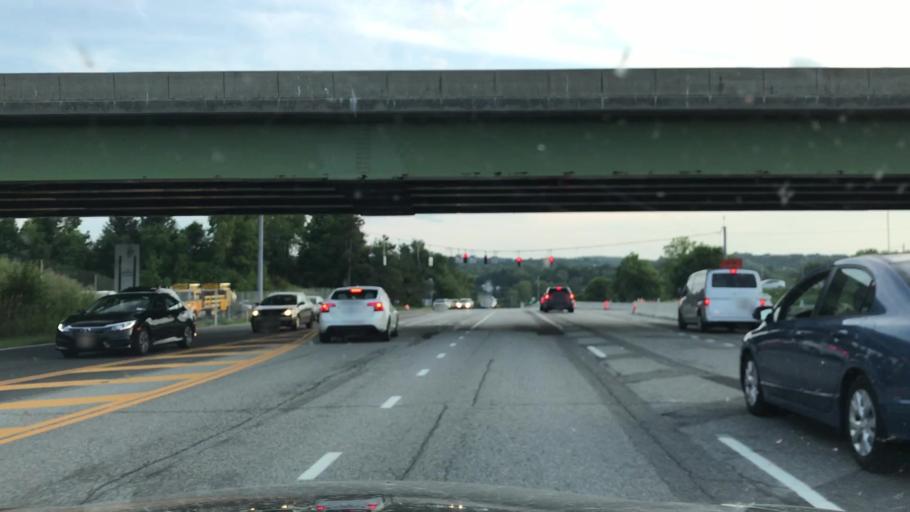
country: US
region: New York
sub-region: Orange County
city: Harriman
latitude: 41.3142
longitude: -74.1368
